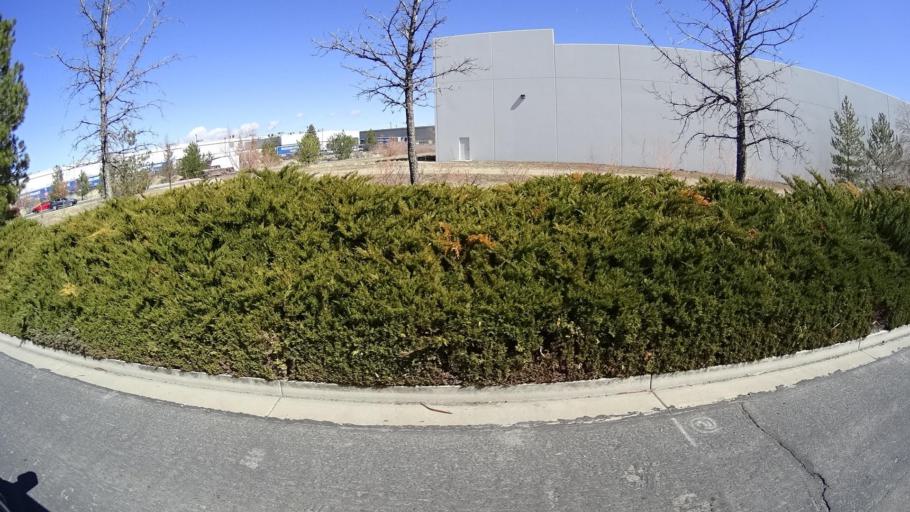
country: US
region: Nevada
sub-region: Washoe County
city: Lemmon Valley
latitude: 39.6471
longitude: -119.8621
